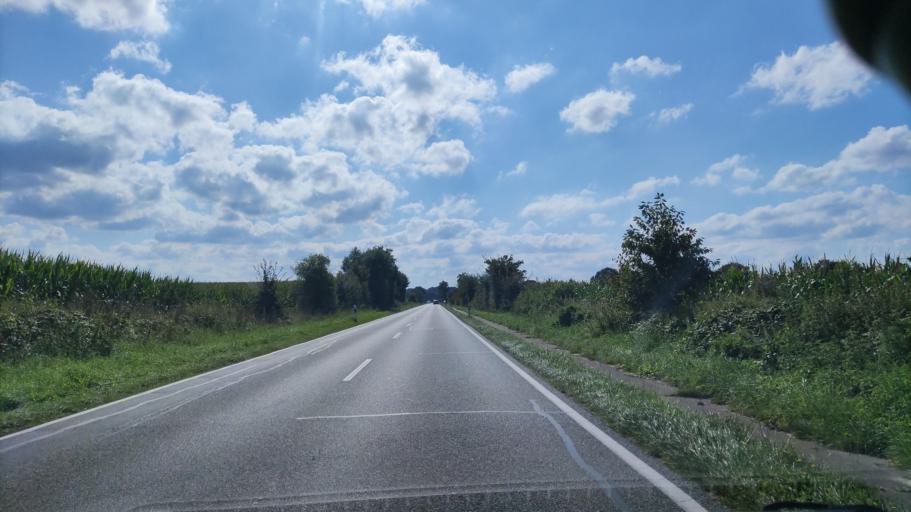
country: DE
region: Schleswig-Holstein
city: Holzbunge
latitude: 54.4036
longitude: 9.6714
